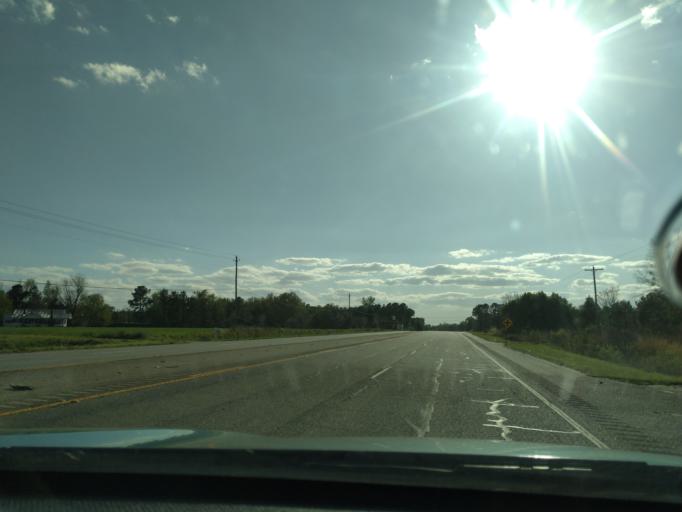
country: US
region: South Carolina
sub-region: Williamsburg County
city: Kingstree
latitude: 33.6392
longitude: -79.9041
